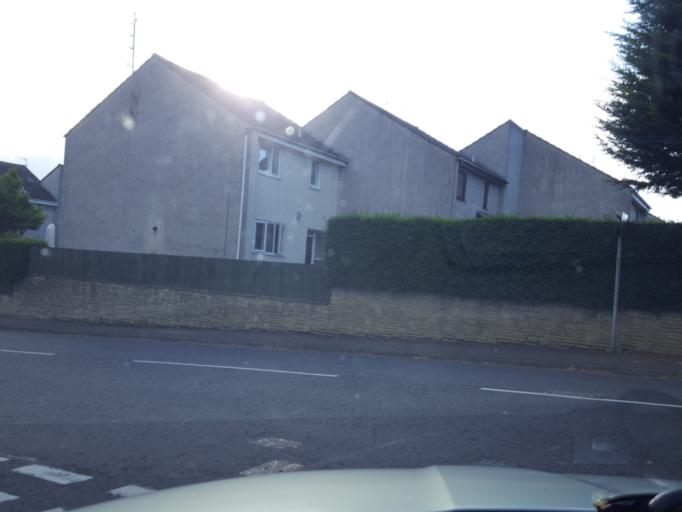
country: GB
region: Scotland
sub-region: Dundee City
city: Dundee
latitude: 56.4556
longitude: -3.0256
